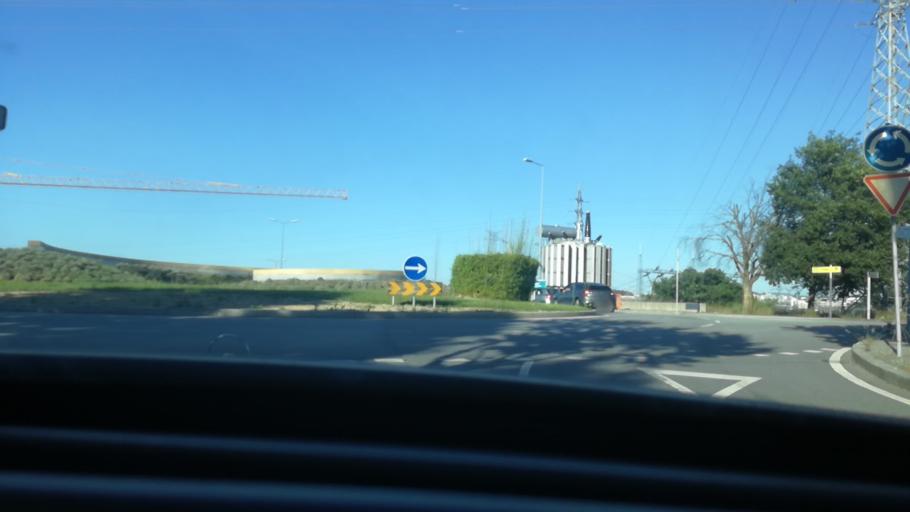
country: PT
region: Porto
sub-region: Maia
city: Maia
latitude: 41.2313
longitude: -8.6080
